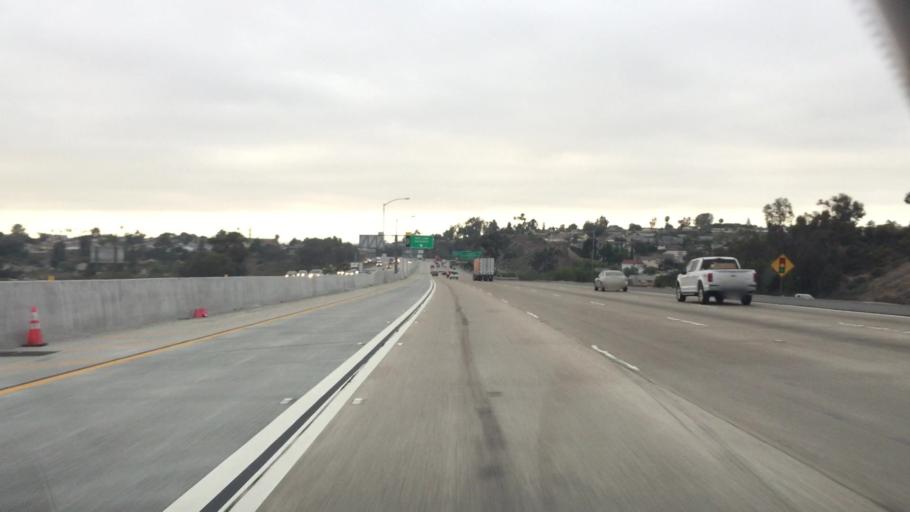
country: US
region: California
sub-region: San Diego County
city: Bonita
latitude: 32.6260
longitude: -117.0423
